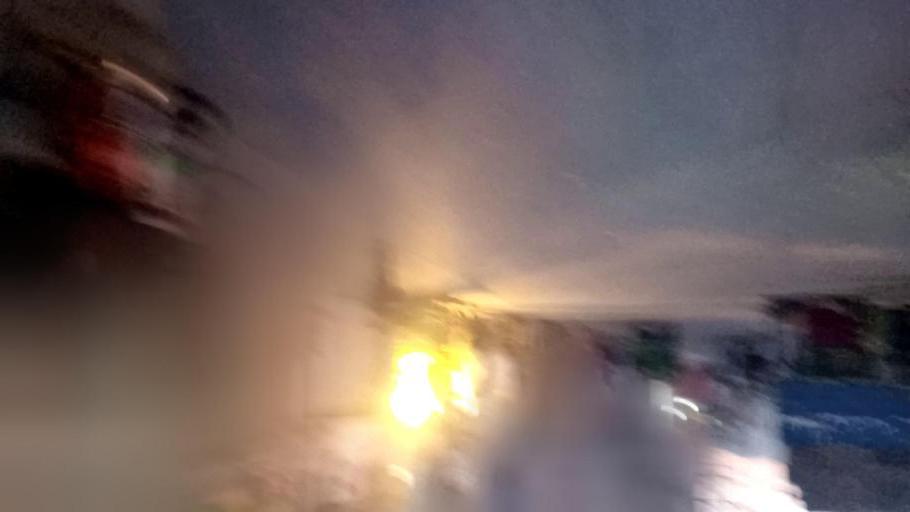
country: PK
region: Khyber Pakhtunkhwa
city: Mingora
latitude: 34.7796
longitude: 72.3435
